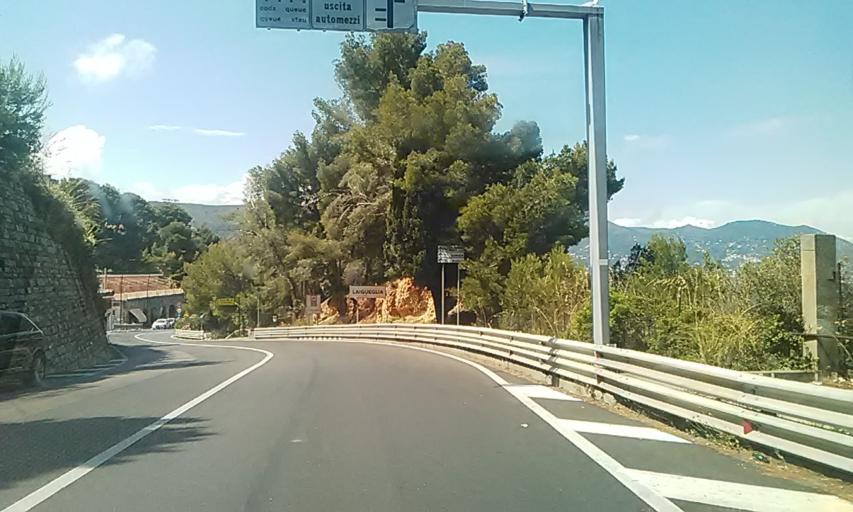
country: IT
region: Liguria
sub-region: Provincia di Savona
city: Laigueglia
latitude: 43.9664
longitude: 8.1649
